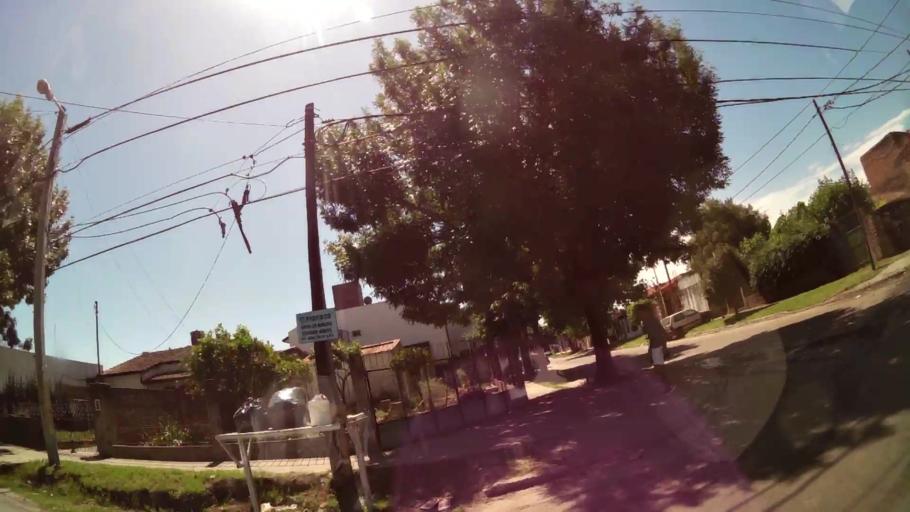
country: AR
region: Buenos Aires
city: Hurlingham
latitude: -34.5013
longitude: -58.6642
